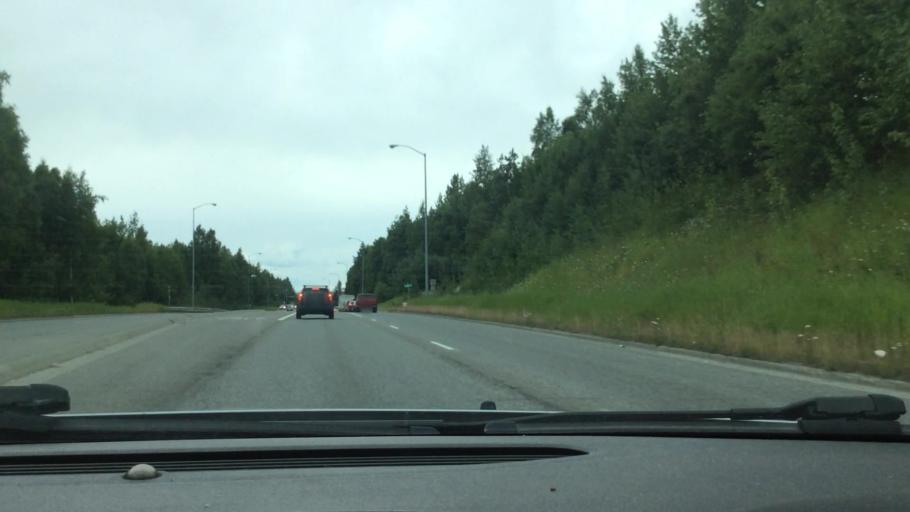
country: US
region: Alaska
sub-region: Anchorage Municipality
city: Anchorage
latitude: 61.2042
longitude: -149.7783
